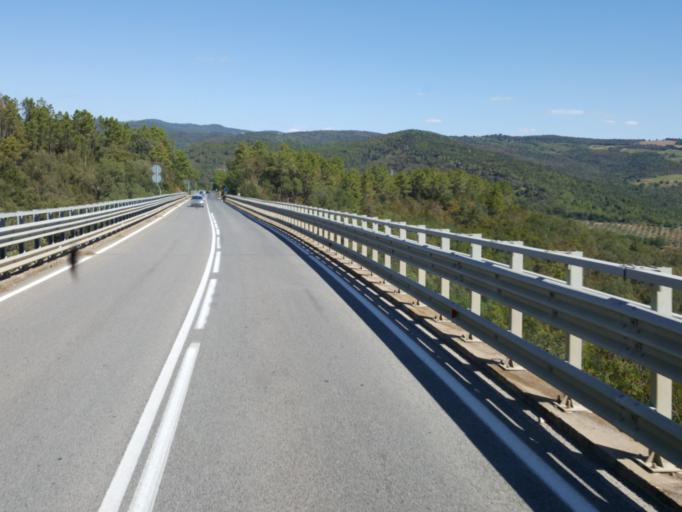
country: IT
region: Tuscany
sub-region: Provincia di Grosseto
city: Civitella Marittima
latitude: 43.0032
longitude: 11.2880
